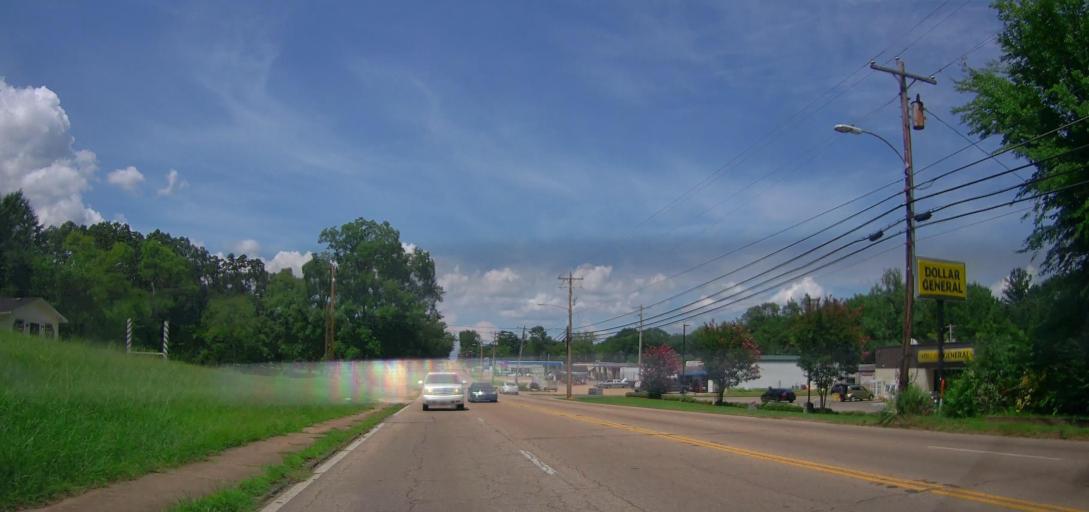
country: US
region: Mississippi
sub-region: Lee County
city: Verona
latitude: 34.1963
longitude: -88.7200
